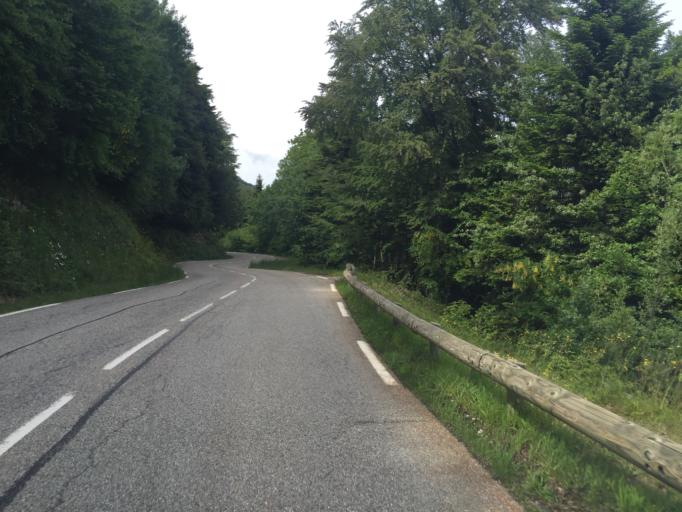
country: FR
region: Rhone-Alpes
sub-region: Departement de la Savoie
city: Saint-Baldoph
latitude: 45.4959
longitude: 5.9180
